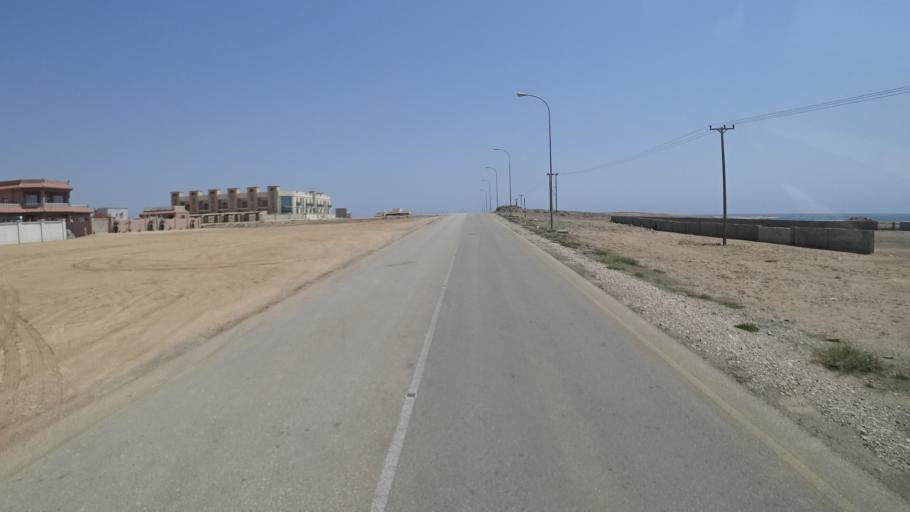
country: OM
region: Zufar
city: Salalah
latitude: 16.9757
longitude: 54.7142
